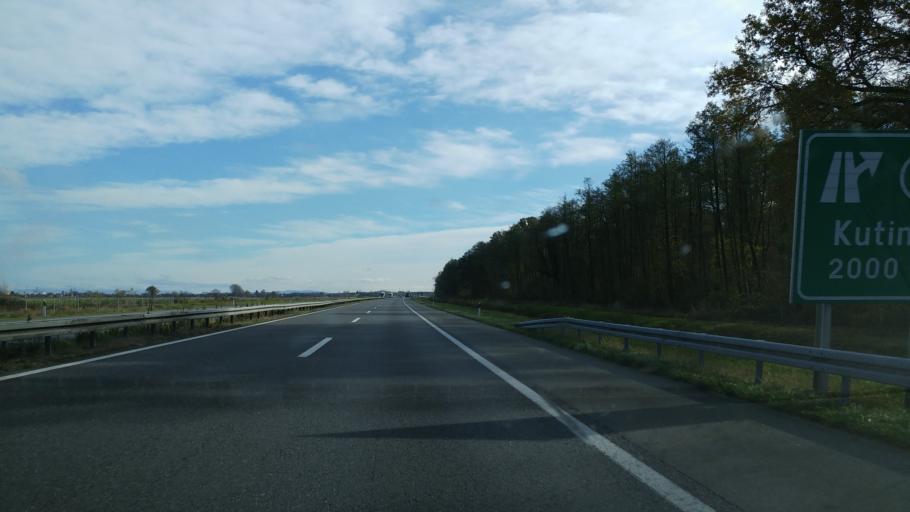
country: HR
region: Sisacko-Moslavacka
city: Repusnica
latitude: 45.4733
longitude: 16.7361
